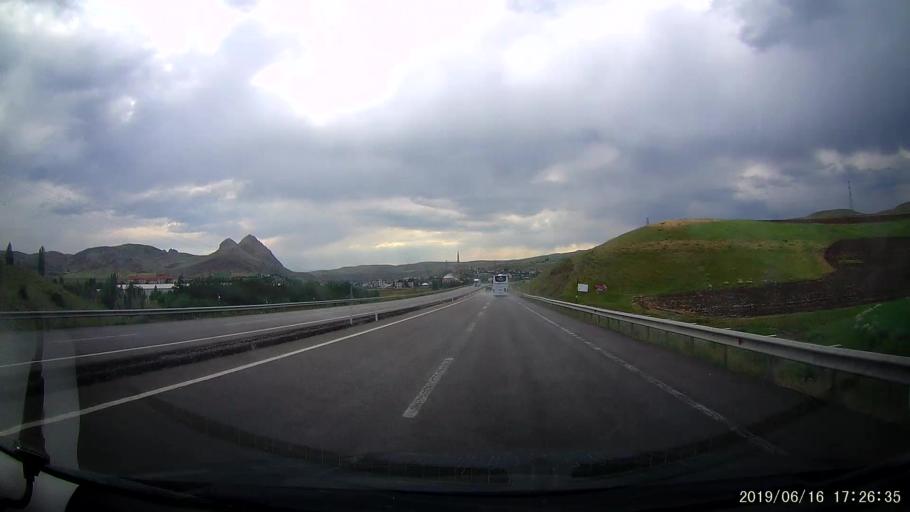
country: TR
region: Erzincan
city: Tercan
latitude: 39.7690
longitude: 40.4091
